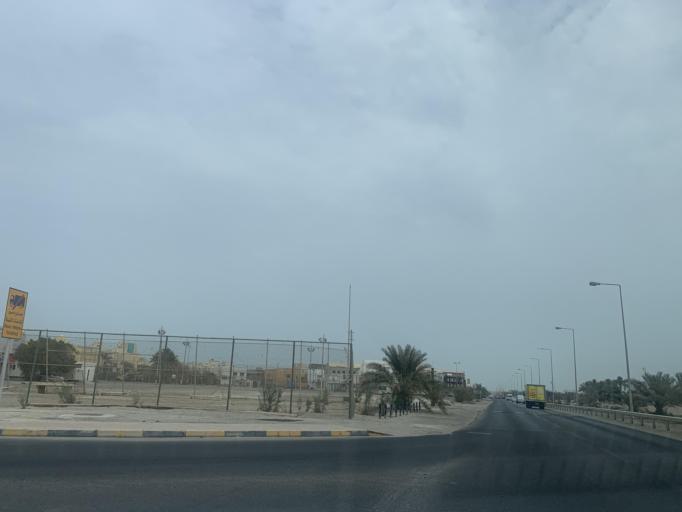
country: BH
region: Muharraq
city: Al Muharraq
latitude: 26.2770
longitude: 50.6335
